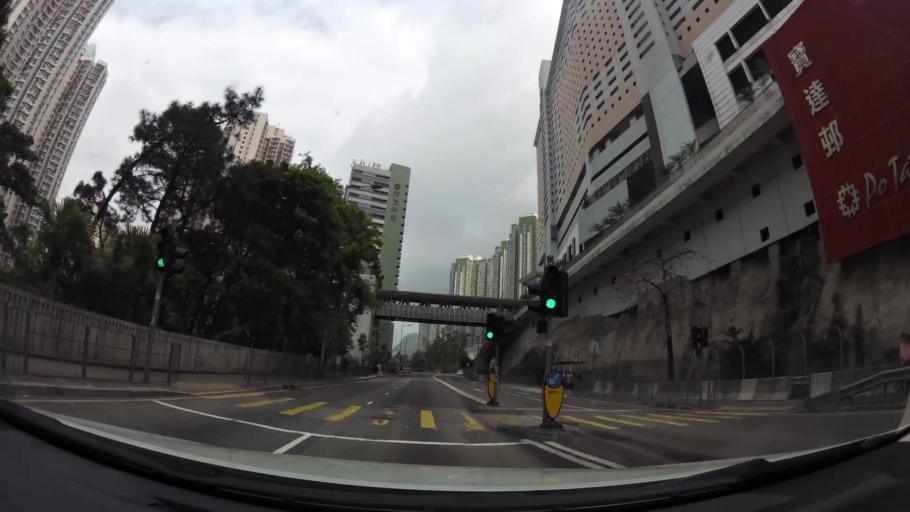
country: HK
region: Kowloon City
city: Kowloon
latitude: 22.3167
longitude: 114.2361
